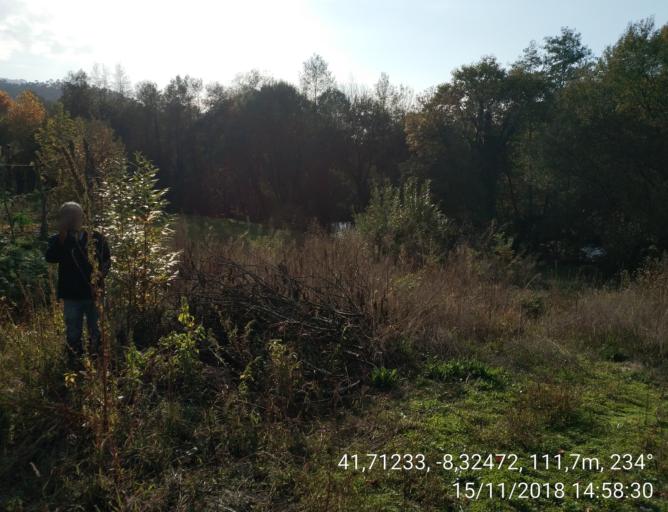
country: PT
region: Braga
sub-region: Terras de Bouro
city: Terras de Bouro
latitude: 41.7123
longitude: -8.3247
